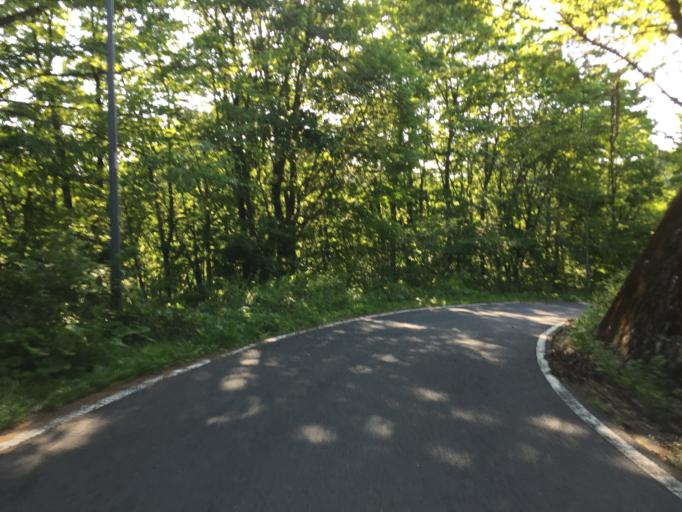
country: JP
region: Ibaraki
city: Kitaibaraki
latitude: 36.9124
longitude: 140.5804
